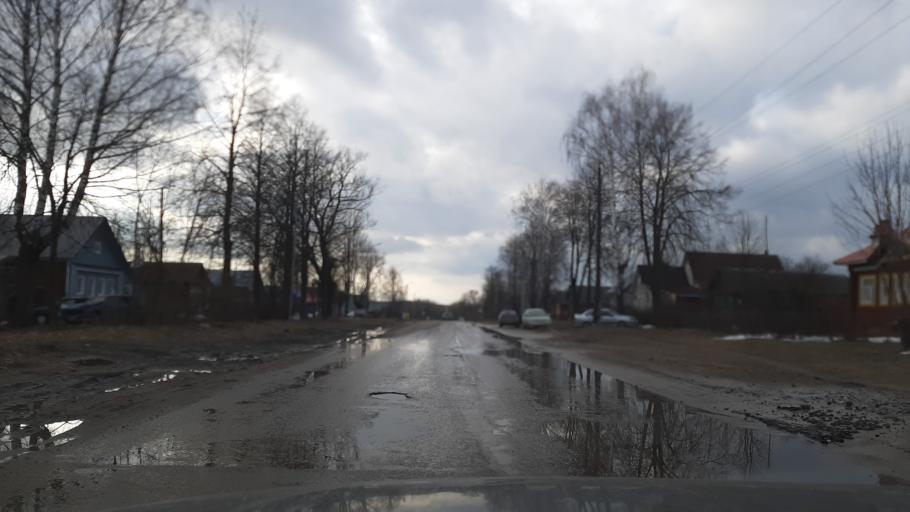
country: RU
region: Ivanovo
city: Teykovo
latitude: 56.8593
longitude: 40.5261
